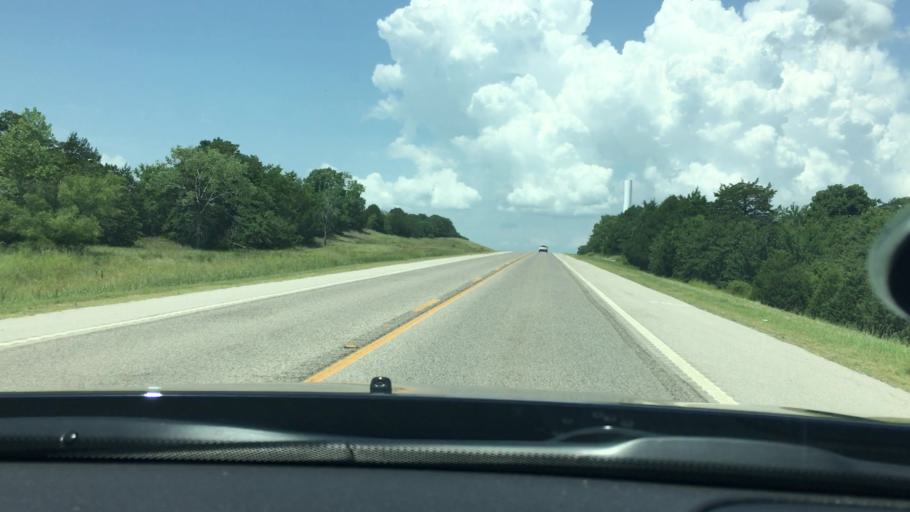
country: US
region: Oklahoma
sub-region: Carter County
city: Dickson
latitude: 34.1003
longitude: -96.9489
